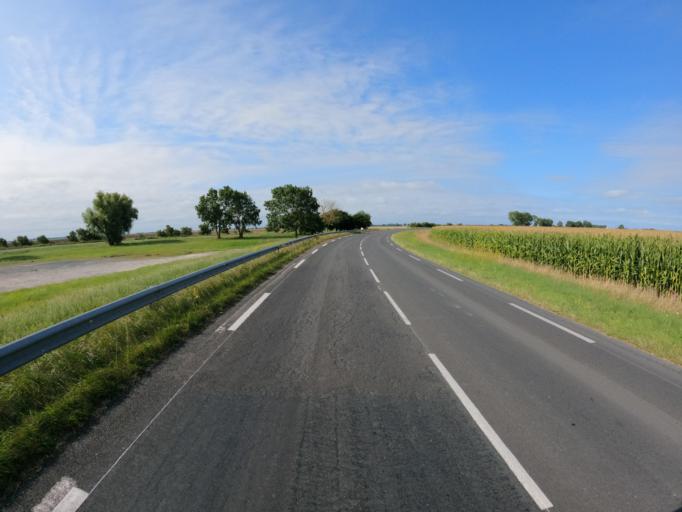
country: FR
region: Pays de la Loire
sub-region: Departement de la Vendee
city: Triaize
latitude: 46.3383
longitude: -1.2646
